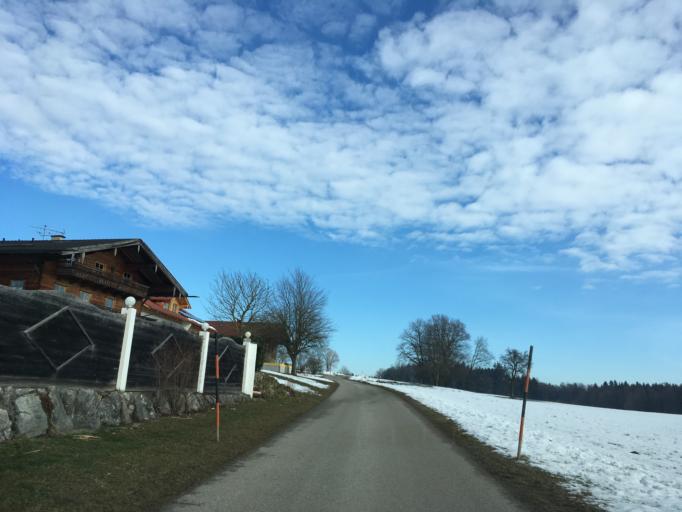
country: DE
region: Bavaria
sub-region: Upper Bavaria
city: Stephanskirchen
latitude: 47.8801
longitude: 12.1597
